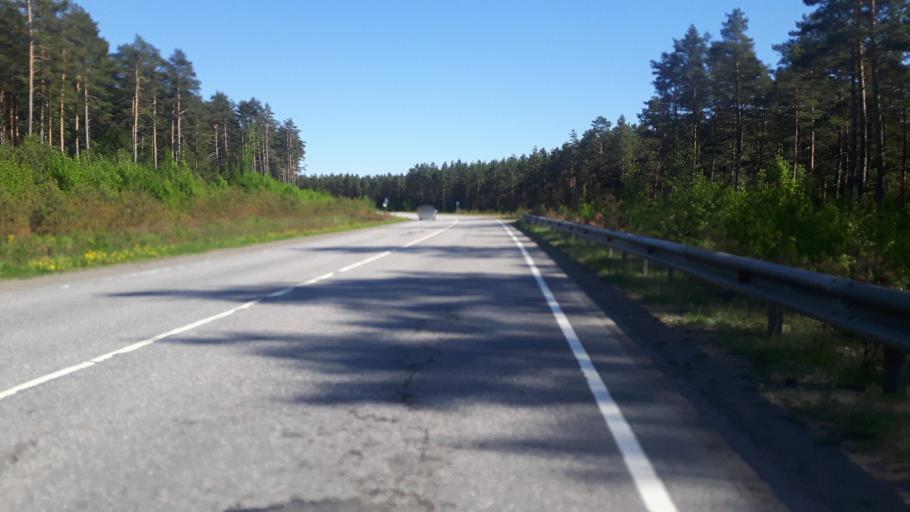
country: RU
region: Leningrad
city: Sosnovyy Bor
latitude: 60.1868
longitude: 29.0249
